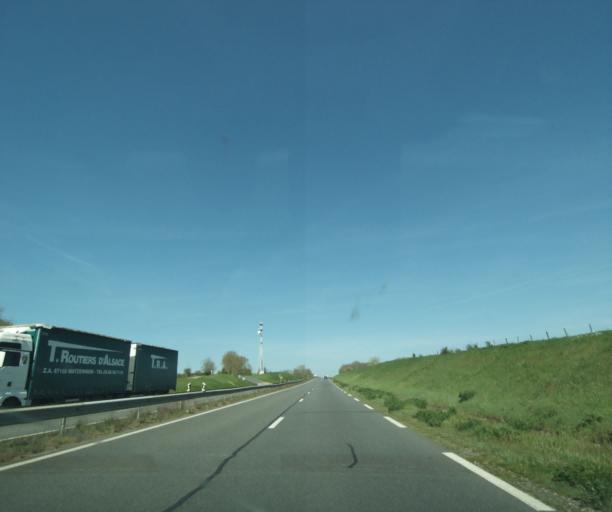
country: FR
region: Bourgogne
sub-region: Departement de la Nievre
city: Saint-Pierre-le-Moutier
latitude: 46.7780
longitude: 3.1303
